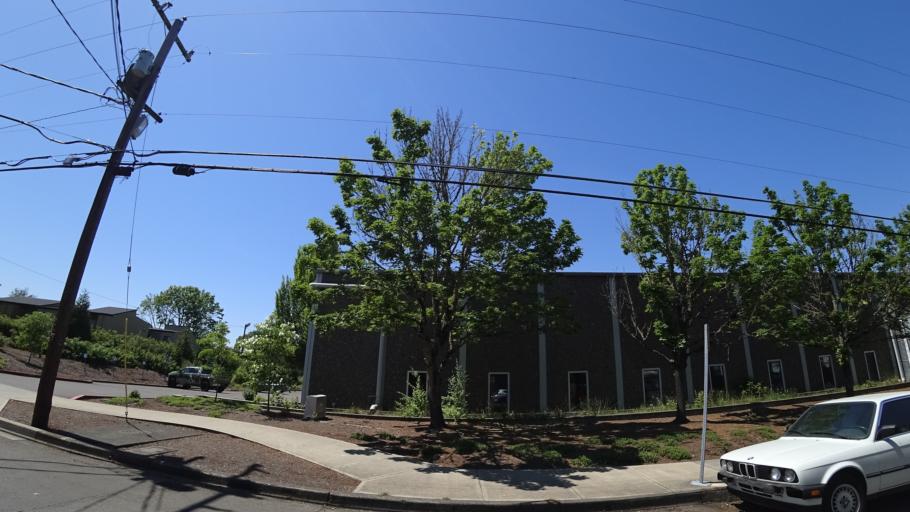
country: US
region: Oregon
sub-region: Washington County
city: Beaverton
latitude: 45.4877
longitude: -122.8224
